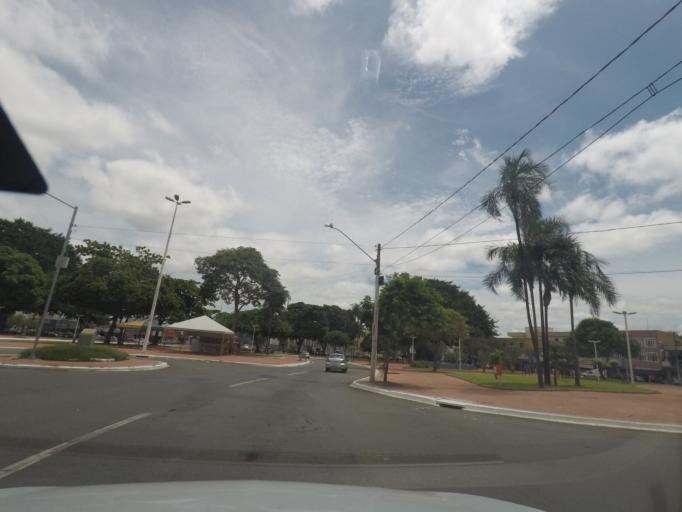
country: BR
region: Goias
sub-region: Goiania
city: Goiania
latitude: -16.6655
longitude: -49.2451
